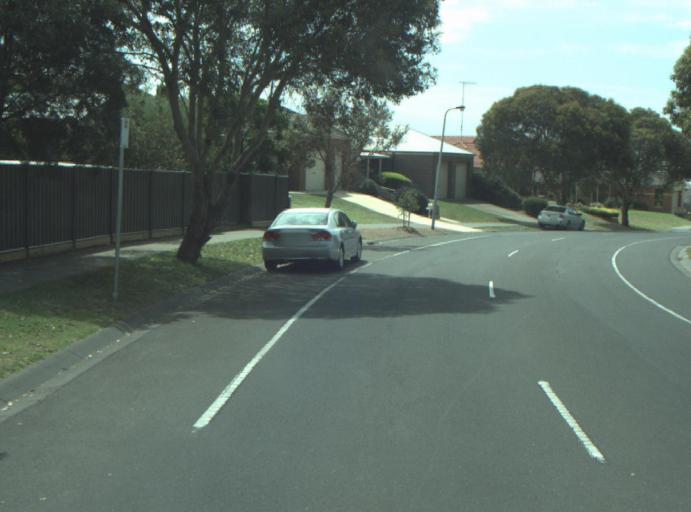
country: AU
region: Victoria
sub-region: Greater Geelong
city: Clifton Springs
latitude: -38.2572
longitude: 144.5475
